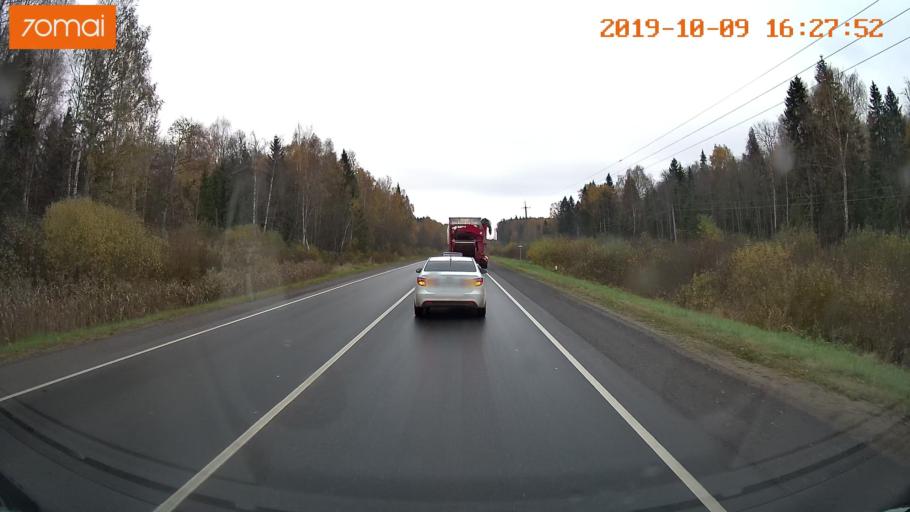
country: RU
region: Kostroma
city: Oktyabr'skiy
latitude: 57.6314
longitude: 40.9297
